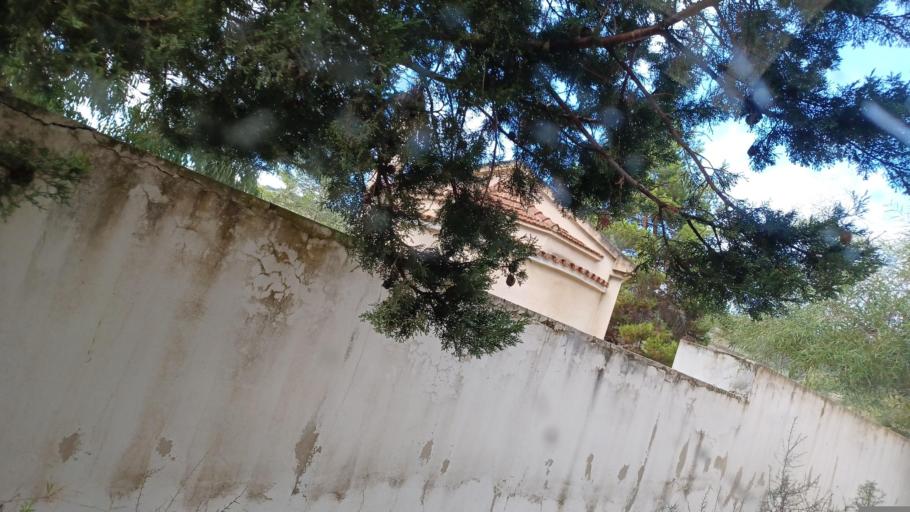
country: CY
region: Pafos
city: Mesogi
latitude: 34.8613
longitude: 32.5081
